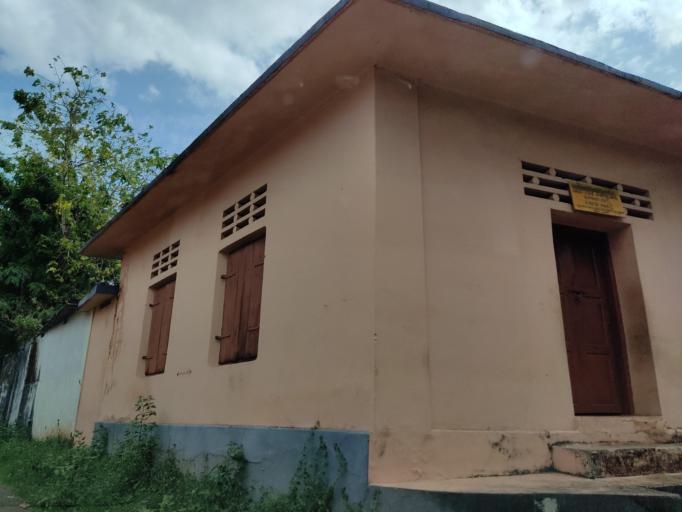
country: IN
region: Kerala
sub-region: Alappuzha
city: Mavelikara
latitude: 9.2520
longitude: 76.5714
